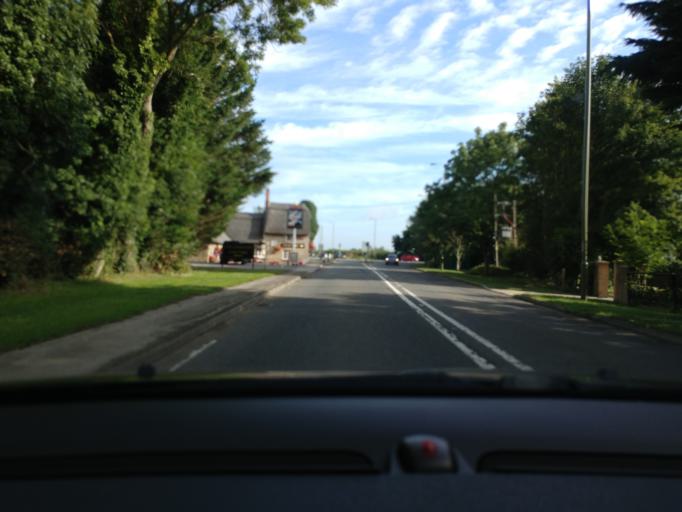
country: GB
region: England
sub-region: Oxfordshire
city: Kidlington
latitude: 51.8566
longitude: -1.2219
